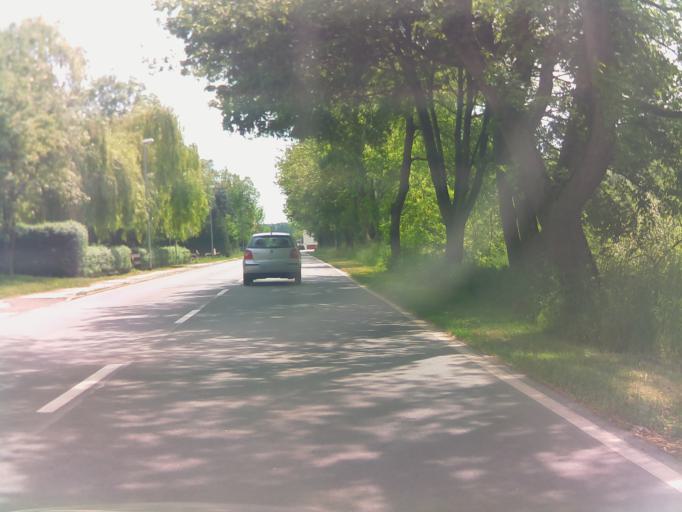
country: DE
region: Saxony-Anhalt
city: Hedersleben
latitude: 51.8514
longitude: 11.2536
